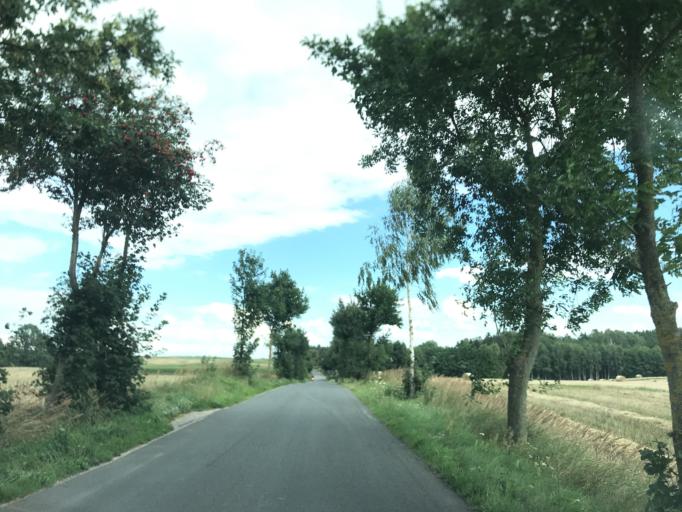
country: PL
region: Kujawsko-Pomorskie
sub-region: Powiat brodnicki
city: Brzozie
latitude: 53.3271
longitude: 19.6851
